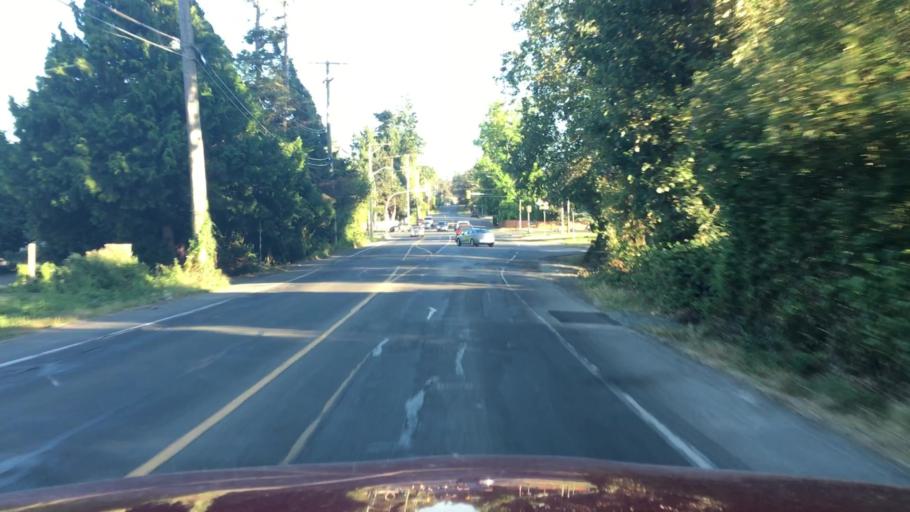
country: CA
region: British Columbia
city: Victoria
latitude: 48.4731
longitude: -123.3516
